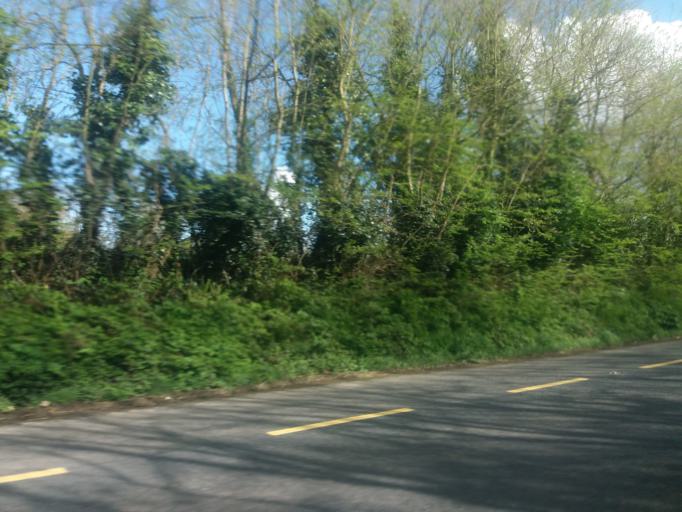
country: IE
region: Leinster
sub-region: Loch Garman
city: Ferns
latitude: 52.5547
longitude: -6.5368
